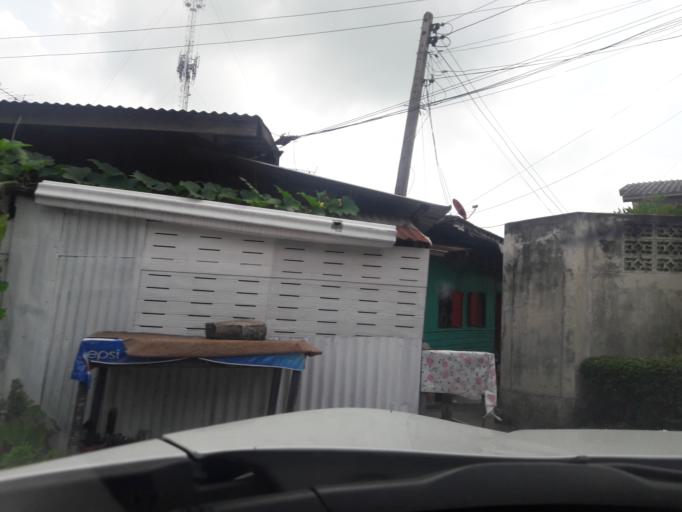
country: TH
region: Lop Buri
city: Ban Mi
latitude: 15.0442
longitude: 100.5436
